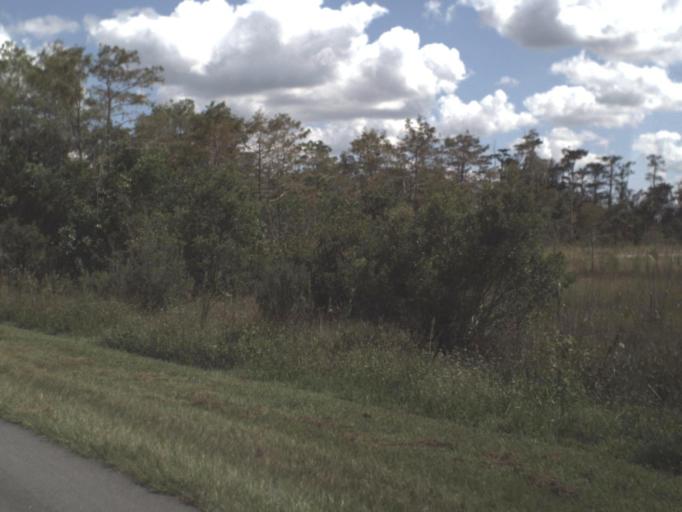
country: US
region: Florida
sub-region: Collier County
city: Lely Resort
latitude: 25.8635
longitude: -81.0990
